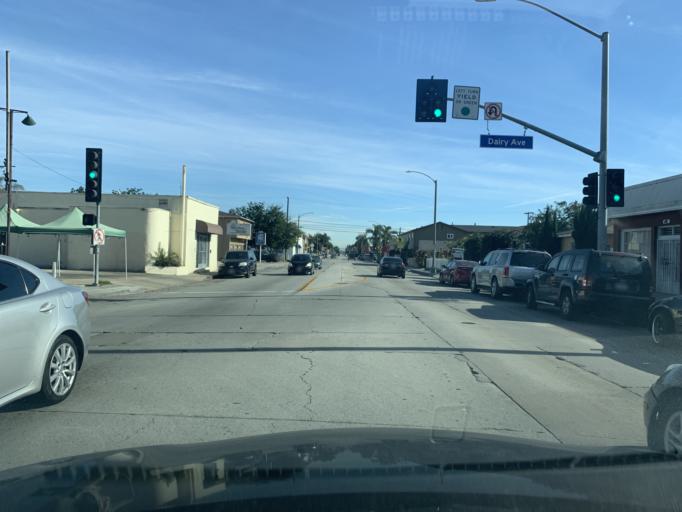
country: US
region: California
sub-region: Los Angeles County
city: East Rancho Dominguez
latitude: 33.8543
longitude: -118.1948
